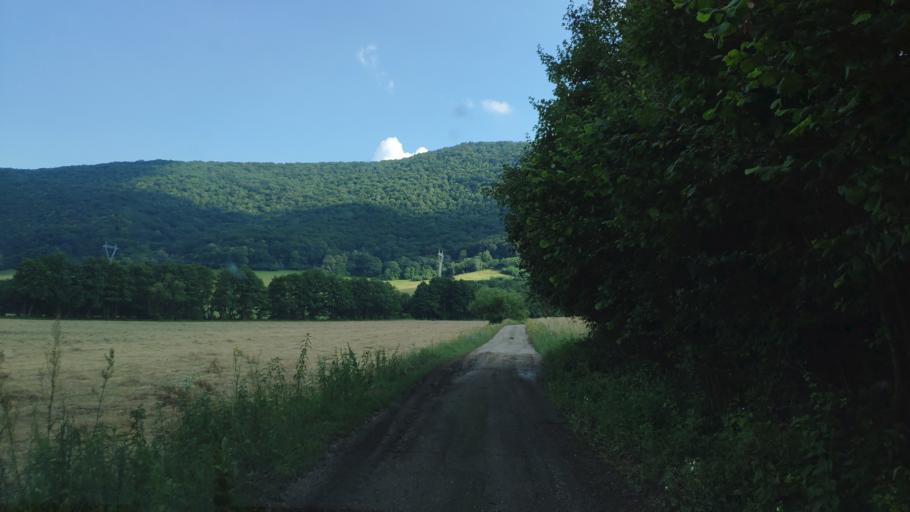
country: HU
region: Borsod-Abauj-Zemplen
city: Szendro
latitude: 48.5887
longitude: 20.7299
